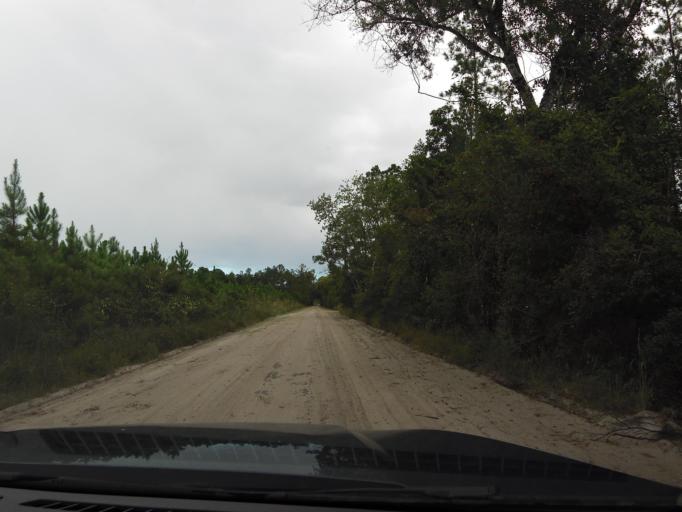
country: US
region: Florida
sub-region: Flagler County
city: Palm Coast
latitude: 29.5891
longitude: -81.3489
